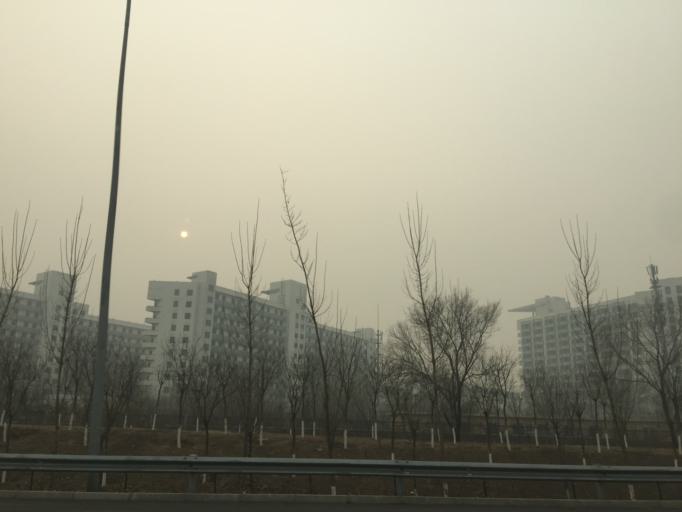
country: CN
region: Beijing
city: Qinghe
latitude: 40.0120
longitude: 116.3269
